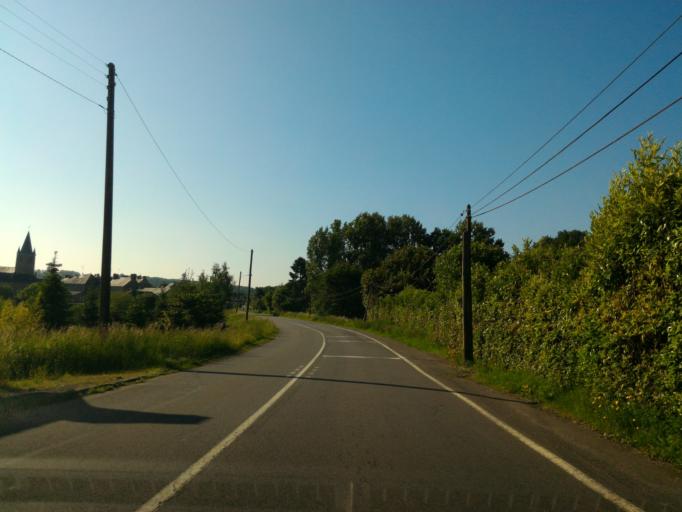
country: FR
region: Brittany
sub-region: Departement d'Ille-et-Vilaine
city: Luitre
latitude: 48.2689
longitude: -1.1468
